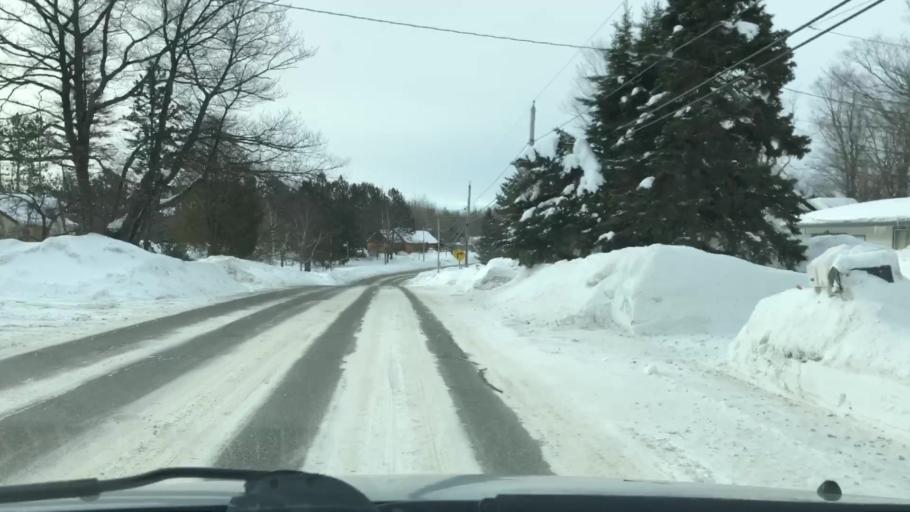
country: US
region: Minnesota
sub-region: Saint Louis County
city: Duluth
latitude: 46.7953
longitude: -92.1494
